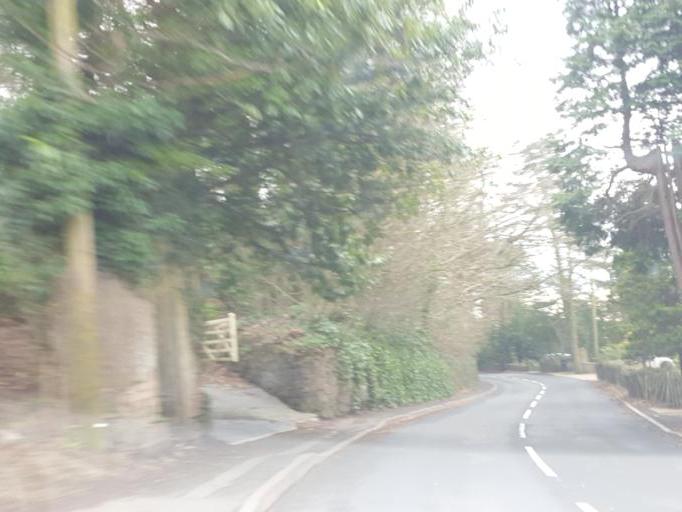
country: GB
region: England
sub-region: Worcestershire
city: Great Malvern
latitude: 52.0954
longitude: -2.3402
